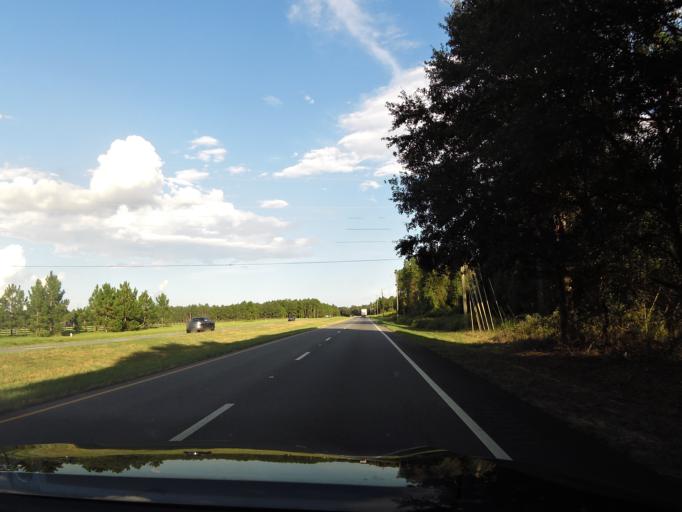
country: US
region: Georgia
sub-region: Lowndes County
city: Remerton
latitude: 30.7998
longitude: -83.3809
